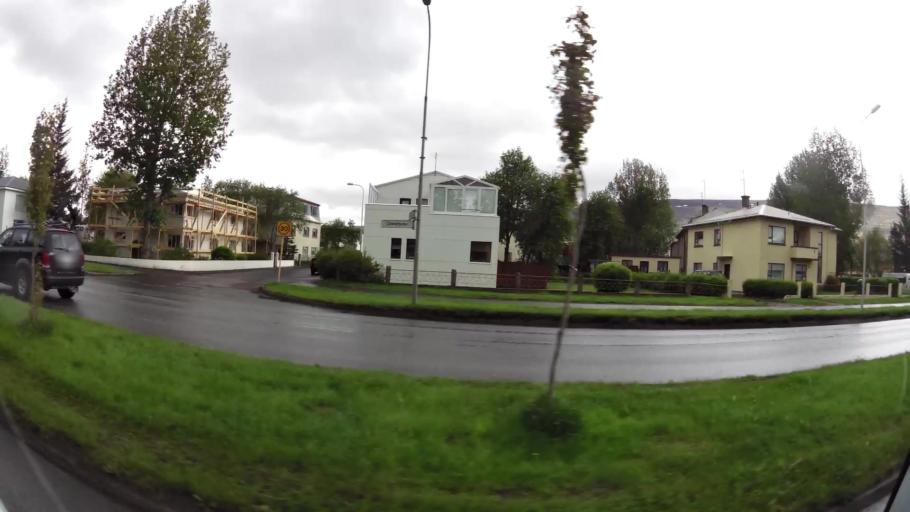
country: IS
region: Northeast
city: Akureyri
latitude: 65.6861
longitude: -18.0927
